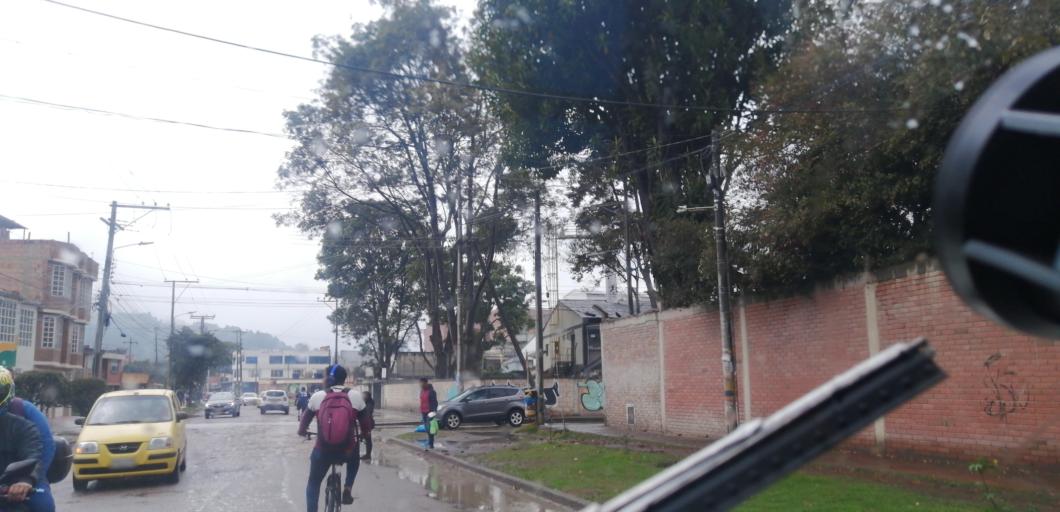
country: CO
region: Cundinamarca
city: Madrid
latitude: 4.7314
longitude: -74.2570
